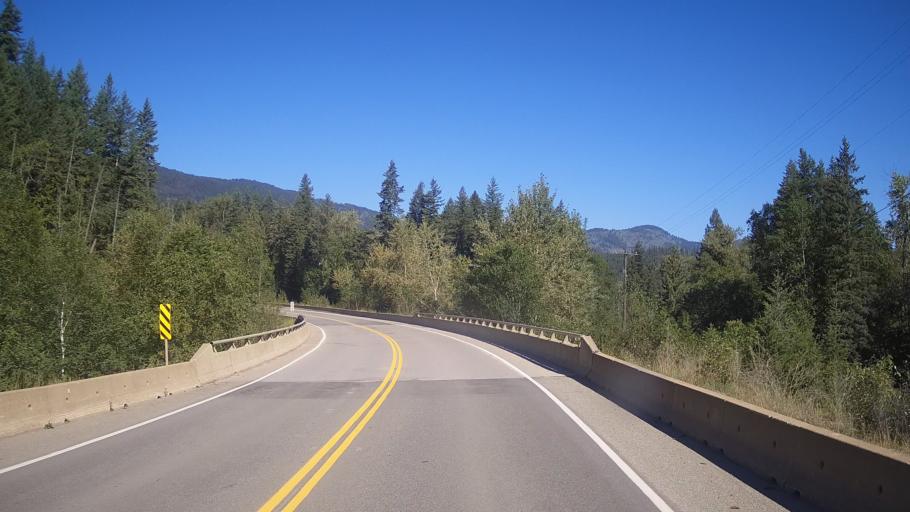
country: CA
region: British Columbia
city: Kamloops
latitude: 51.4529
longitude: -120.2162
